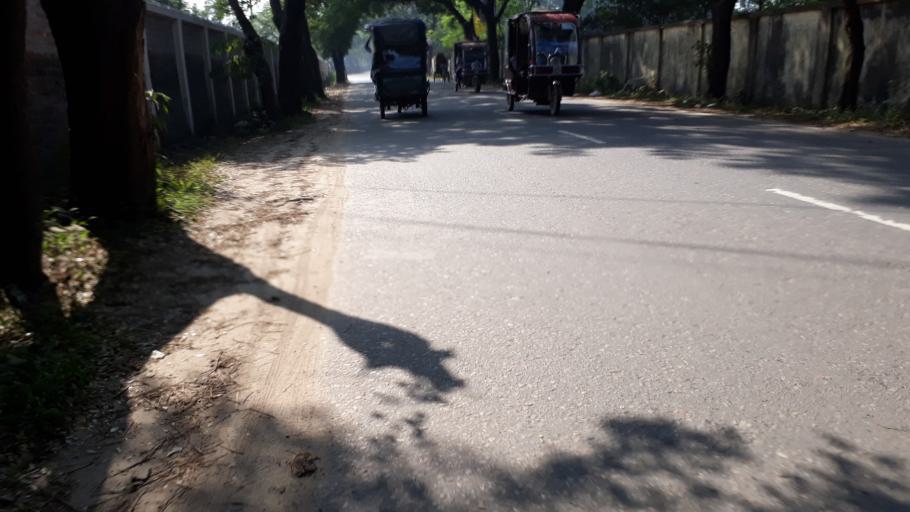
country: BD
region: Dhaka
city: Tungi
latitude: 23.8987
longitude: 90.2739
